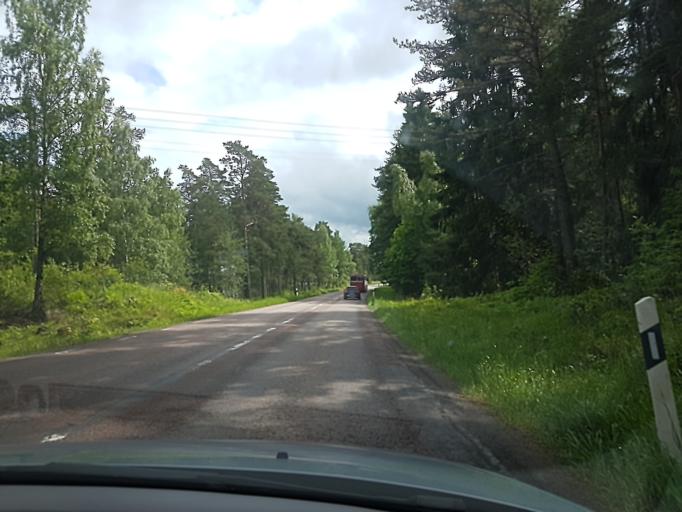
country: SE
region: Uppsala
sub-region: Osthammars Kommun
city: OEsthammar
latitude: 60.2522
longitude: 18.3473
